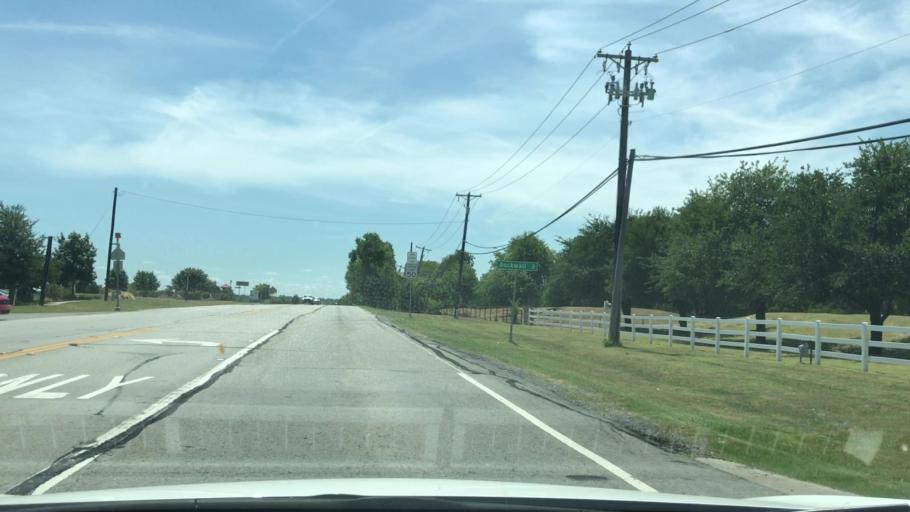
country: US
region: Texas
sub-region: Rockwall County
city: Rockwall
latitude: 32.9643
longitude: -96.4648
